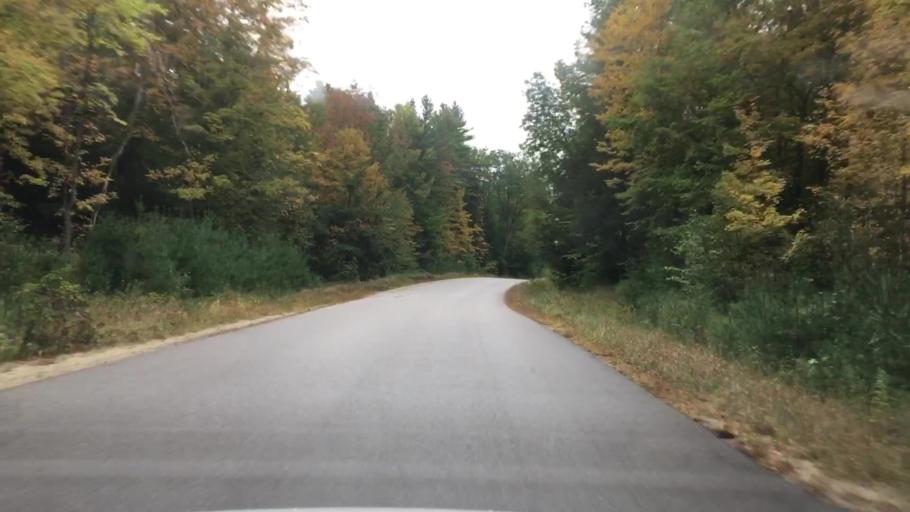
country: US
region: Maine
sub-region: Cumberland County
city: Harrison
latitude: 44.0219
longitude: -70.5889
